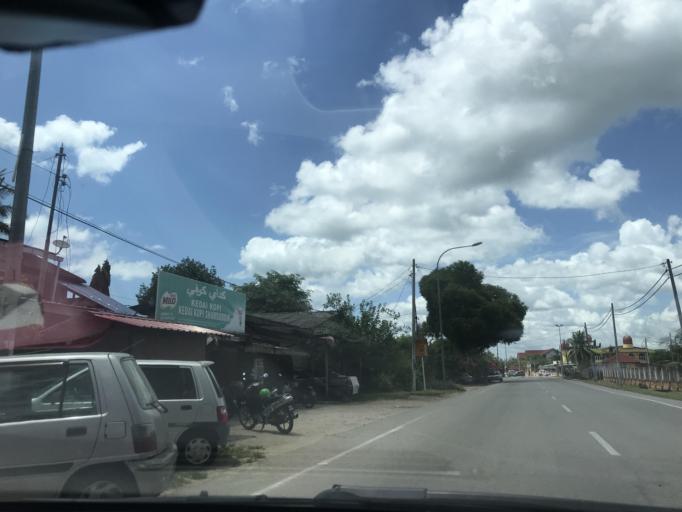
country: TH
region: Narathiwat
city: Tak Bai
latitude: 6.2317
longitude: 102.0936
